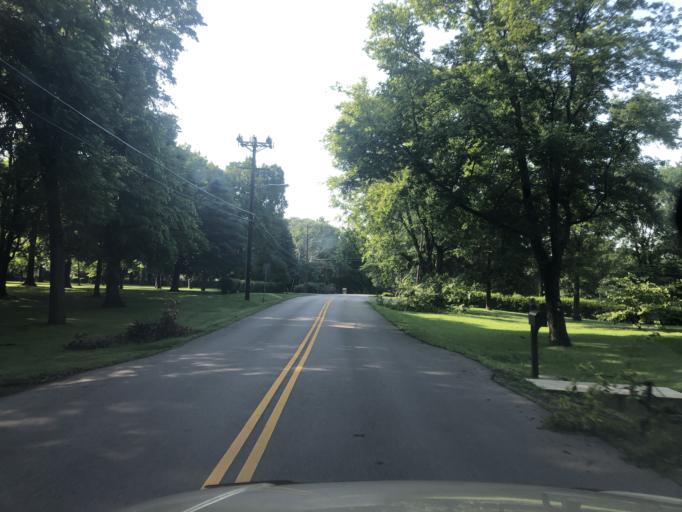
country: US
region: Tennessee
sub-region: Davidson County
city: Lakewood
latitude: 36.2262
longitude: -86.7114
